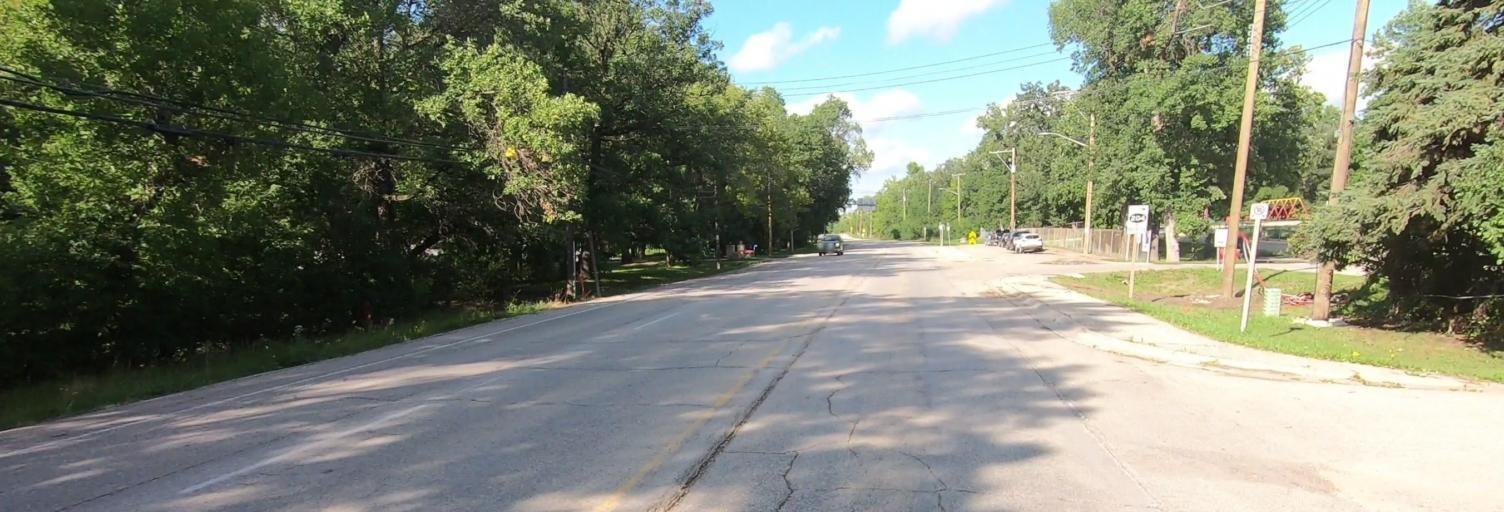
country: CA
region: Manitoba
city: Winnipeg
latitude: 49.9911
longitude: -97.0405
